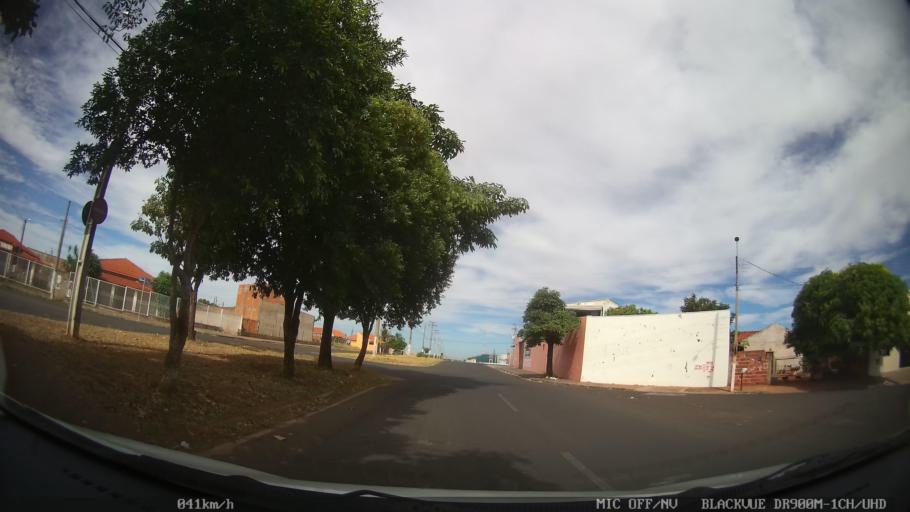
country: BR
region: Sao Paulo
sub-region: Catanduva
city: Catanduva
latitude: -21.1670
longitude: -48.9697
